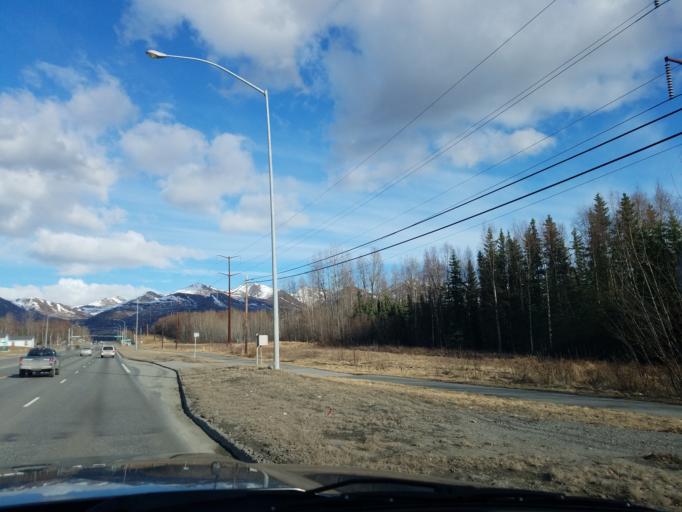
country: US
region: Alaska
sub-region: Anchorage Municipality
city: Anchorage
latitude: 61.1807
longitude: -149.7703
